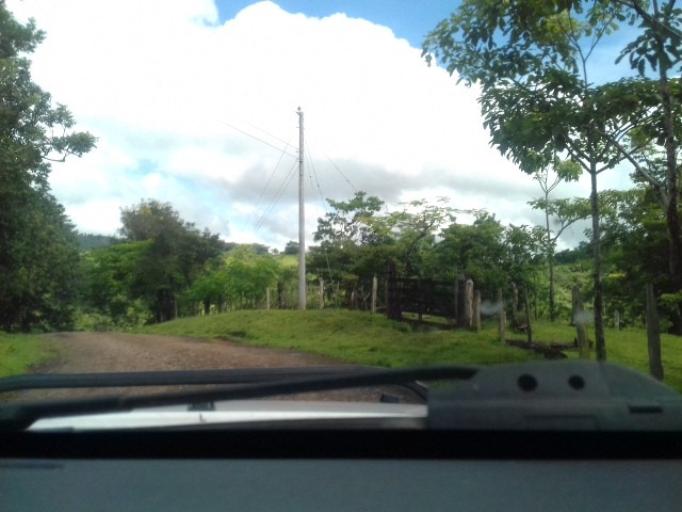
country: NI
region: Matagalpa
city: Rio Blanco
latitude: 12.9774
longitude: -85.1840
